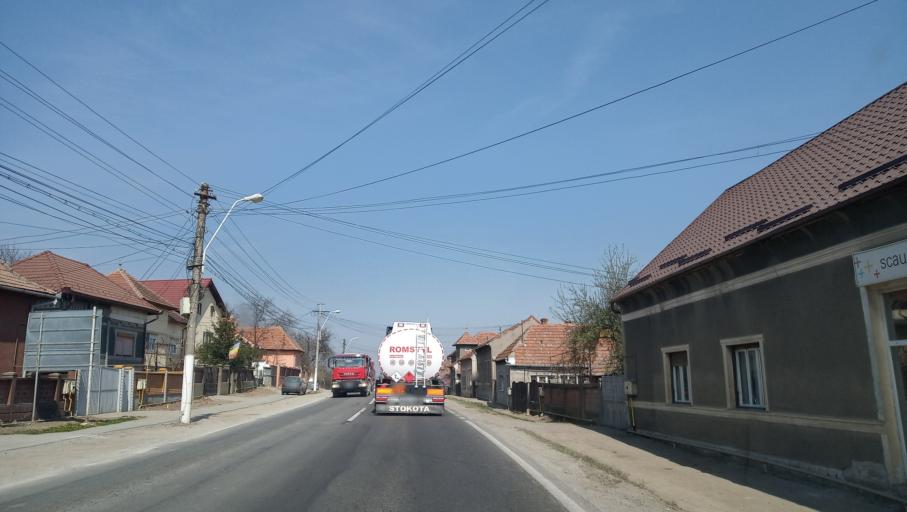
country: RO
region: Alba
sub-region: Oras Teius
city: Teius
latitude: 46.2105
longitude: 23.6767
